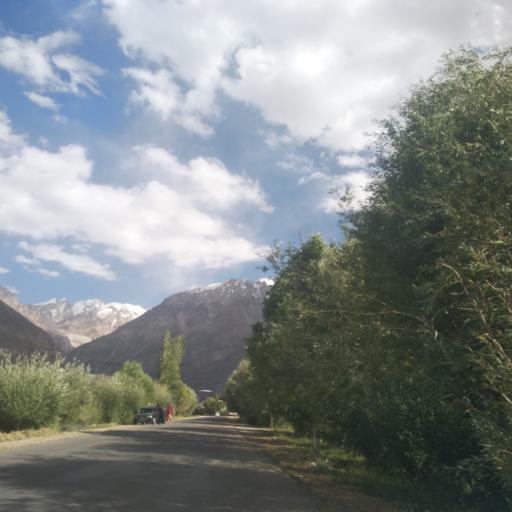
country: TJ
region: Gorno-Badakhshan
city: Roshtqal'a
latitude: 37.7256
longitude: 72.1607
